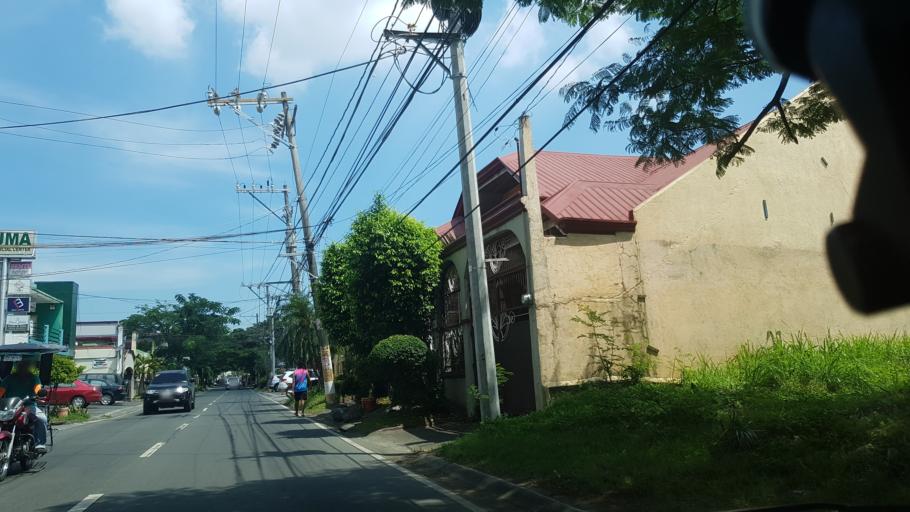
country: PH
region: Calabarzon
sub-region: Province of Rizal
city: Las Pinas
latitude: 14.4311
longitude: 120.9943
